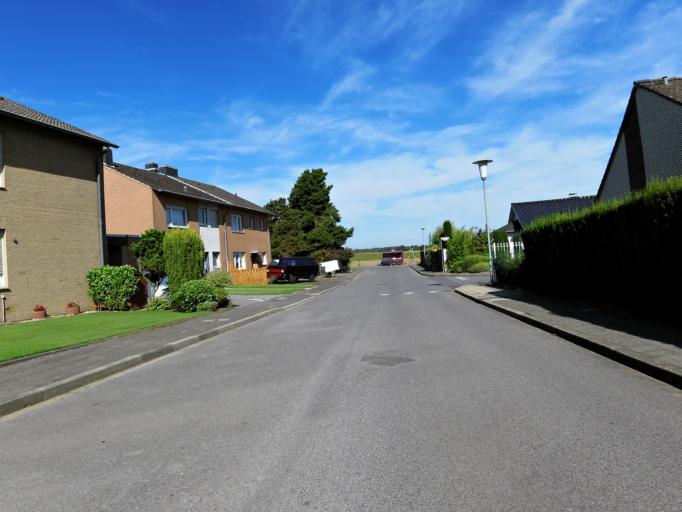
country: DE
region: North Rhine-Westphalia
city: Siersdorf
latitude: 50.8478
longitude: 6.2239
